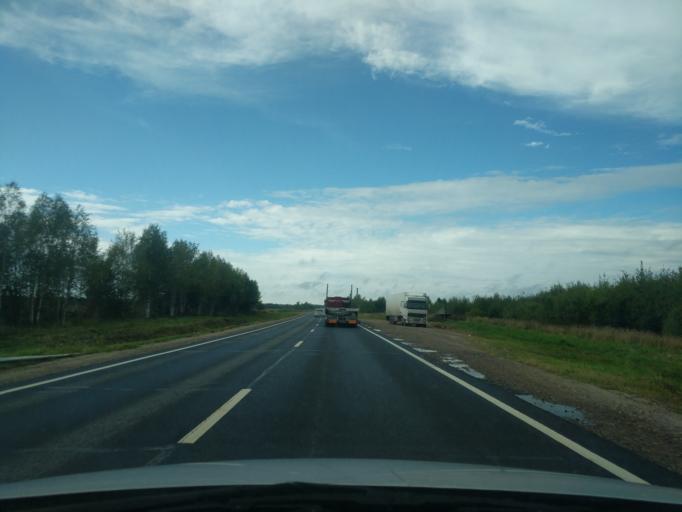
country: RU
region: Kostroma
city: Sudislavl'
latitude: 57.8163
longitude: 41.9636
